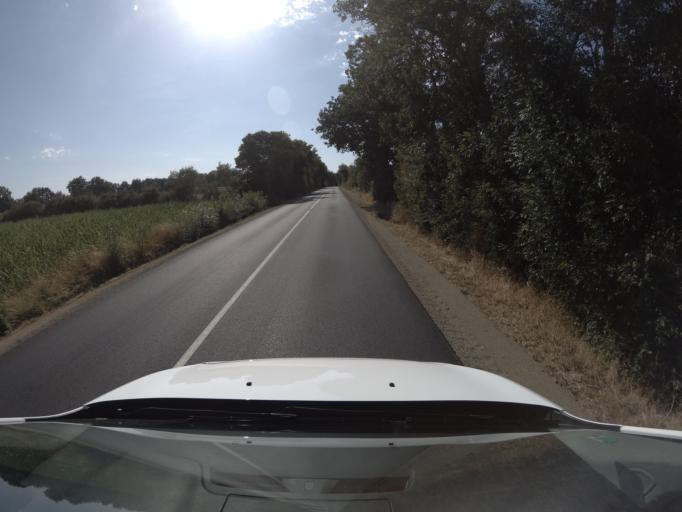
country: FR
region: Poitou-Charentes
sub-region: Departement des Deux-Sevres
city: Mauze-Thouarsais
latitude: 46.9993
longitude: -0.3253
